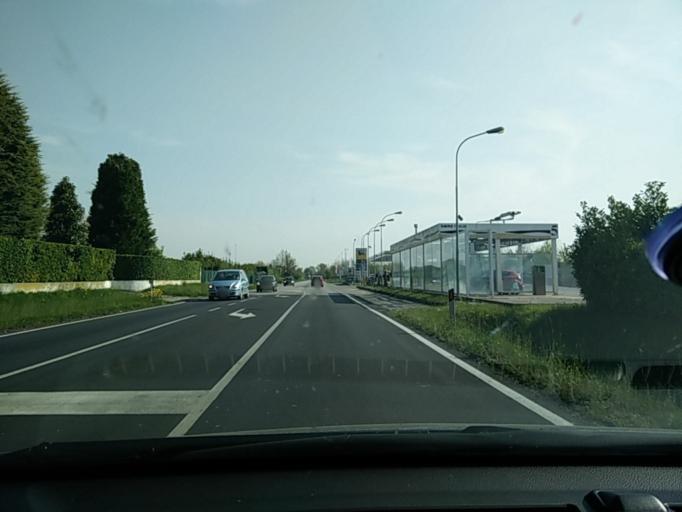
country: IT
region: Friuli Venezia Giulia
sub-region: Provincia di Pordenone
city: Azzano Decimo
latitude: 45.9215
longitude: 12.6364
